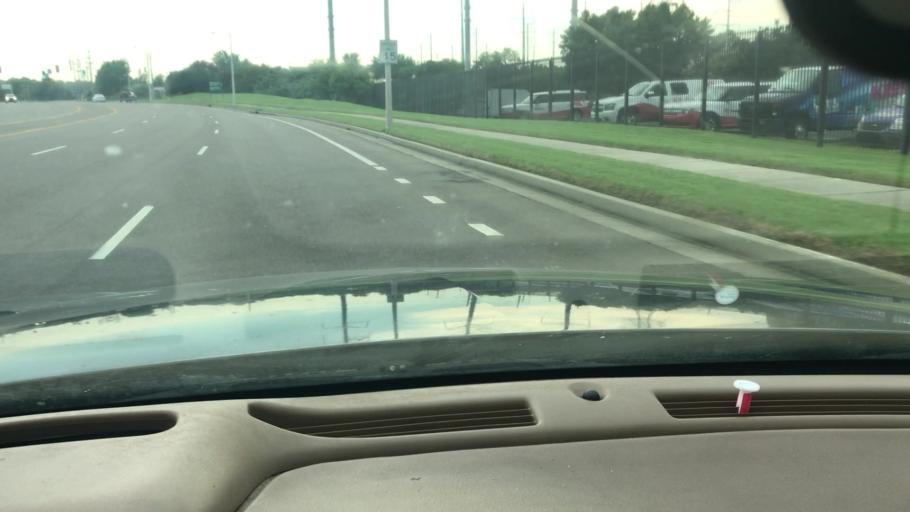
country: US
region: Tennessee
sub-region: Shelby County
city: Germantown
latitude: 35.0752
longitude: -89.8997
